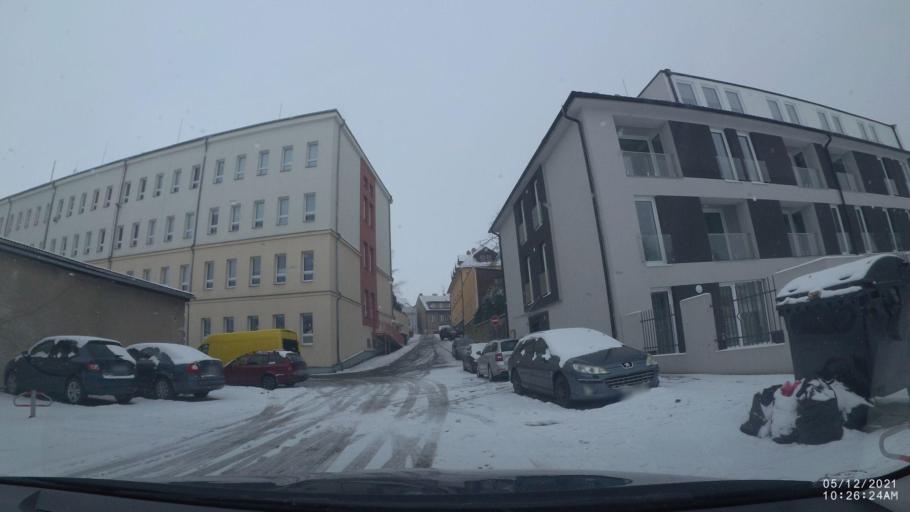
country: CZ
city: Vamberk
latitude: 50.1167
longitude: 16.2885
